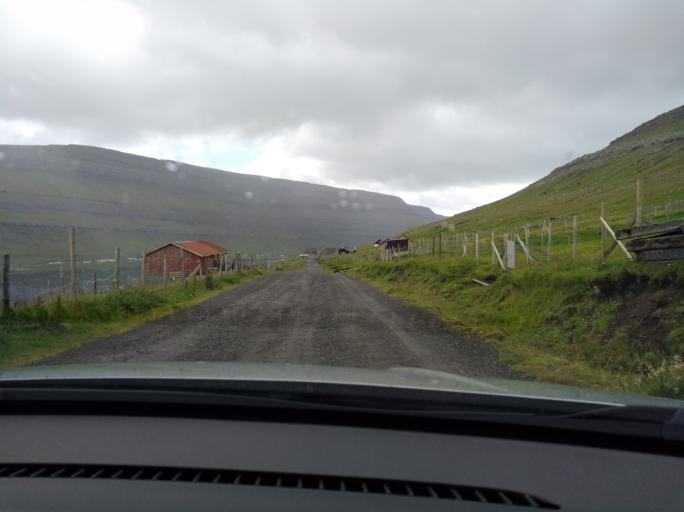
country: FO
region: Nordoyar
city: Klaksvik
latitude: 62.2199
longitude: -6.5880
